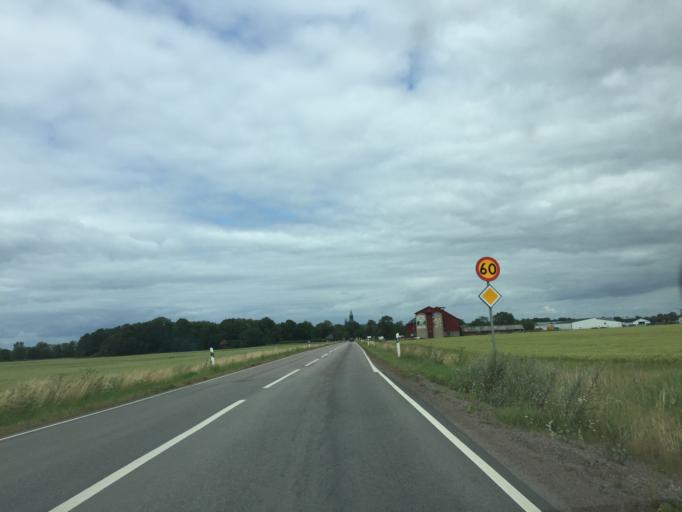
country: SE
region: OEstergoetland
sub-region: Vadstena Kommun
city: Vadstena
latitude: 58.4353
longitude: 14.8772
